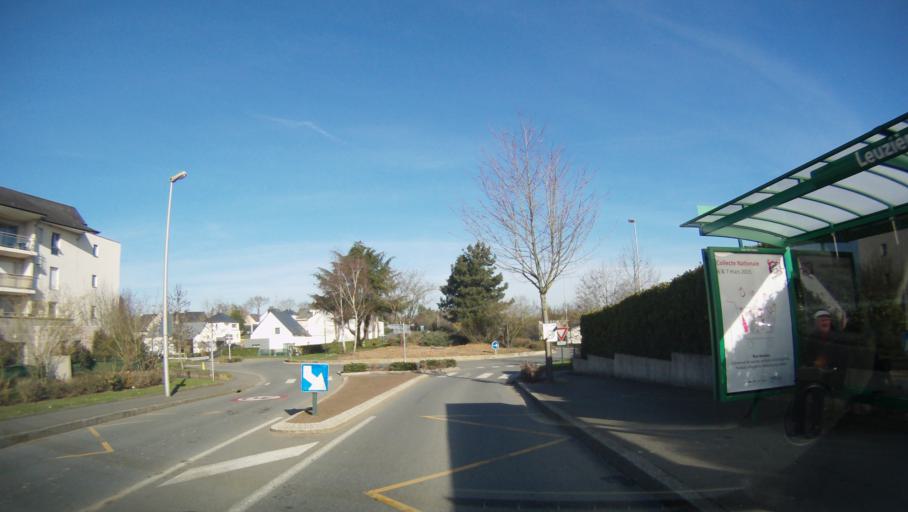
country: FR
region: Brittany
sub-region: Departement d'Ille-et-Vilaine
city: Saint-Erblon
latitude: 48.0215
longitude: -1.6536
